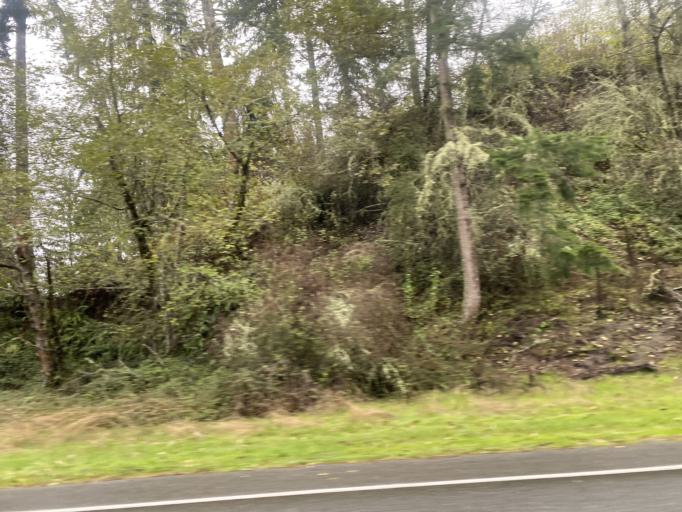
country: US
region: Washington
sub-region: Island County
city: Langley
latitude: 48.0487
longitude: -122.4436
